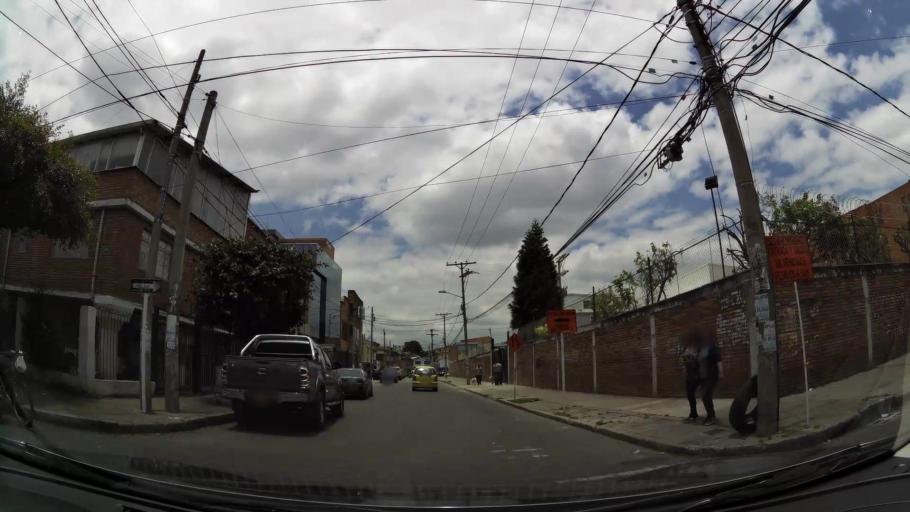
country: CO
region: Bogota D.C.
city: Barrio San Luis
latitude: 4.7185
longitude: -74.0564
